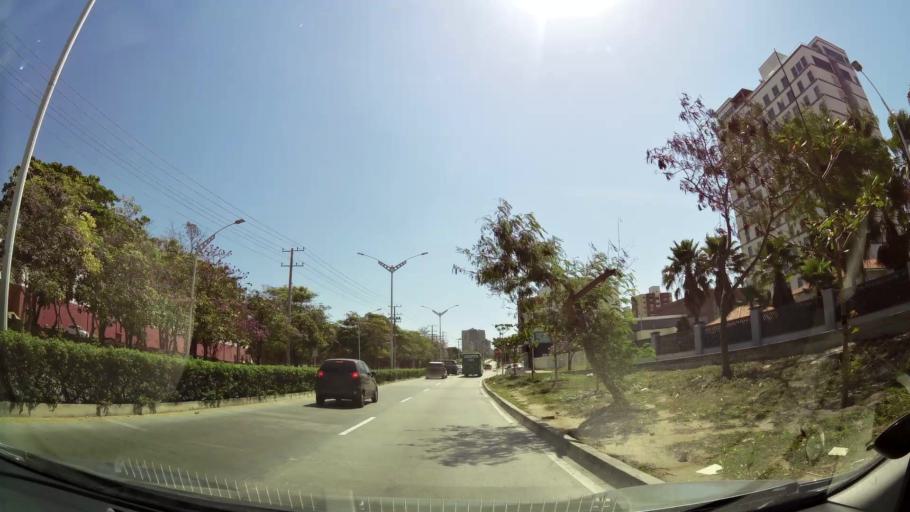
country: CO
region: Atlantico
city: Barranquilla
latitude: 11.0151
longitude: -74.8372
